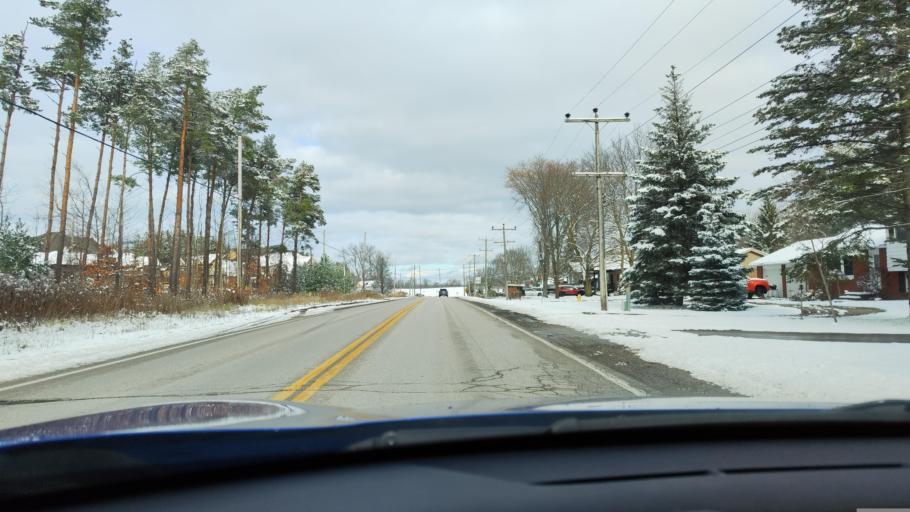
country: CA
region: Ontario
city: Barrie
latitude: 44.3890
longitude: -79.7561
